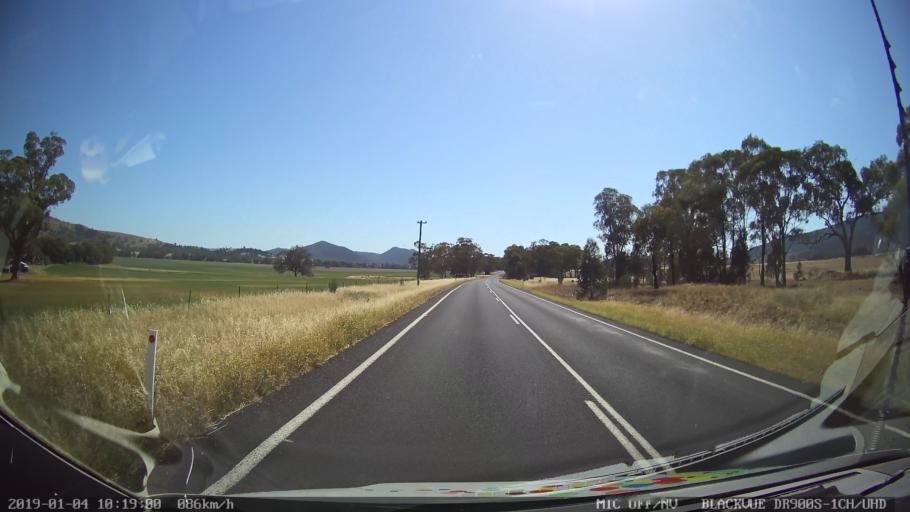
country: AU
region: New South Wales
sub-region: Cabonne
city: Canowindra
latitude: -33.3790
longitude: 148.4743
